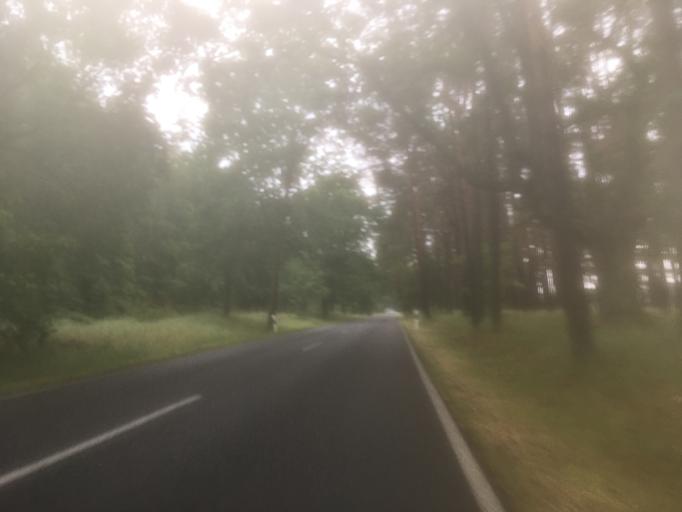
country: DE
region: Brandenburg
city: Zehdenick
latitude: 53.0180
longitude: 13.3387
